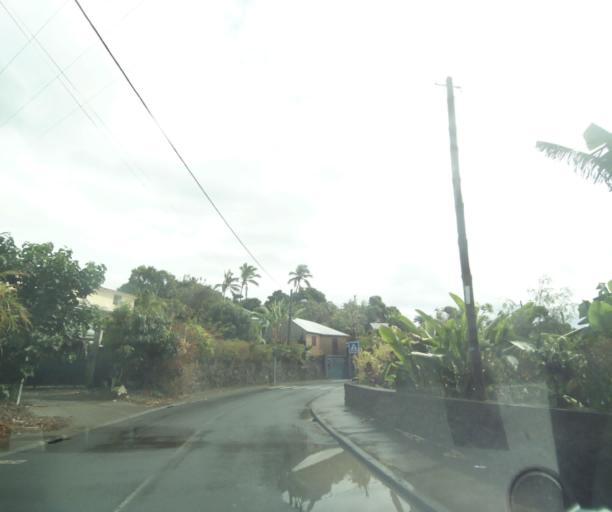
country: RE
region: Reunion
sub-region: Reunion
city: Saint-Paul
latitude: -21.0051
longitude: 55.3227
